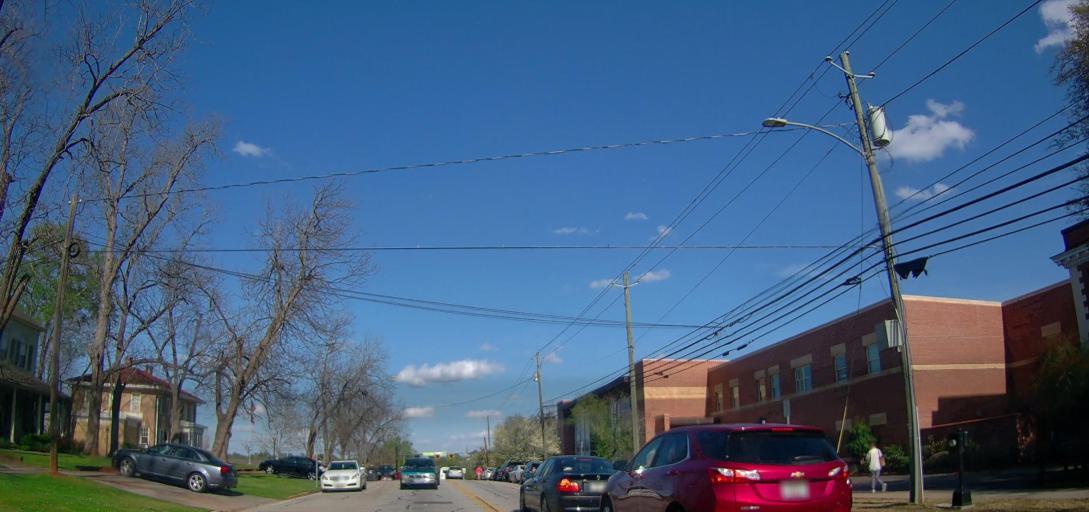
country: US
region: Georgia
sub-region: Baldwin County
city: Milledgeville
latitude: 33.0831
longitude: -83.2326
